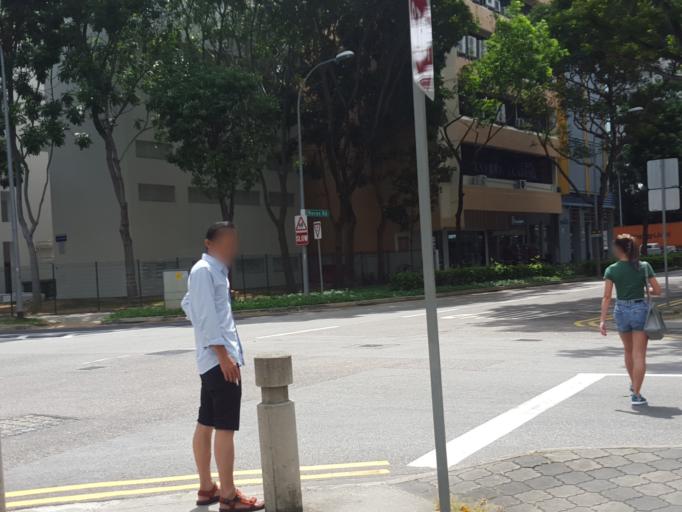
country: SG
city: Singapore
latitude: 1.3089
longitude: 103.8622
